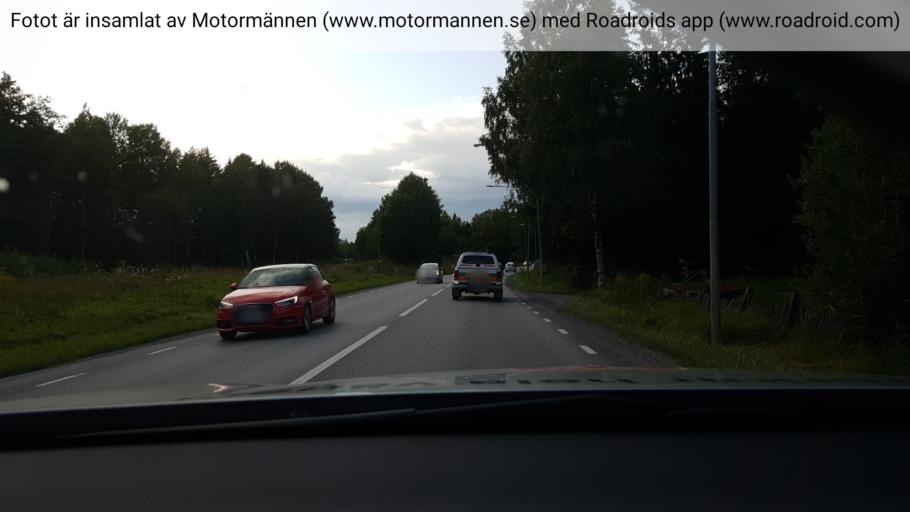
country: SE
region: Stockholm
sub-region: Botkyrka Kommun
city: Fittja
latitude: 59.2407
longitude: 17.8996
